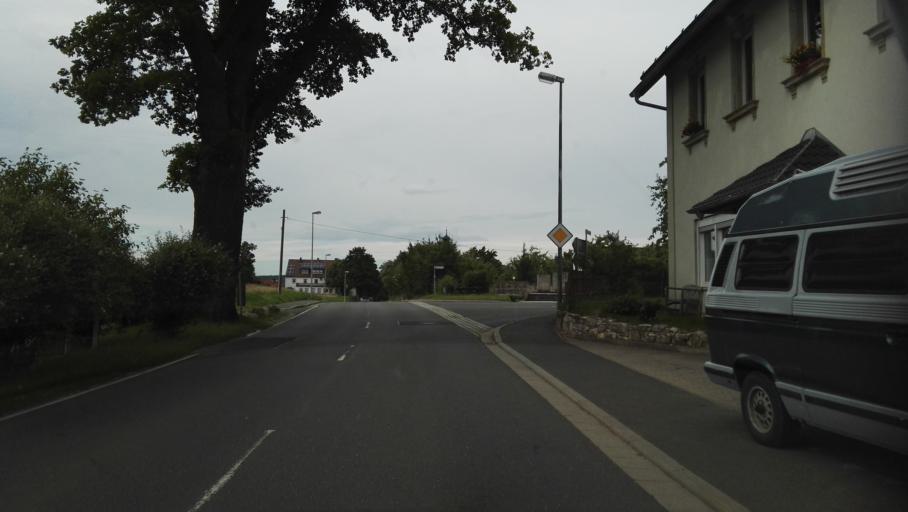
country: DE
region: Bavaria
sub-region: Upper Franconia
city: Plankenfels
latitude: 49.8854
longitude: 11.3344
